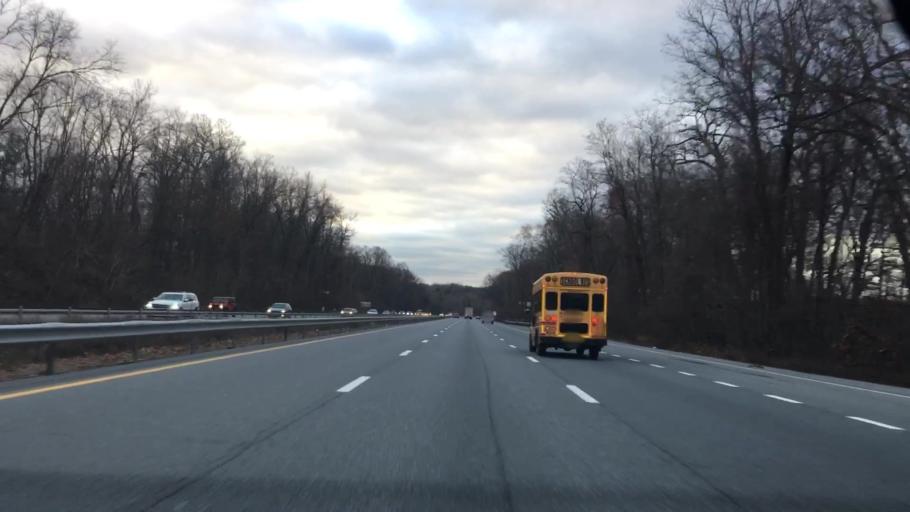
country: US
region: New York
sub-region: Westchester County
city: Purchase
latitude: 41.0752
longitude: -73.7186
